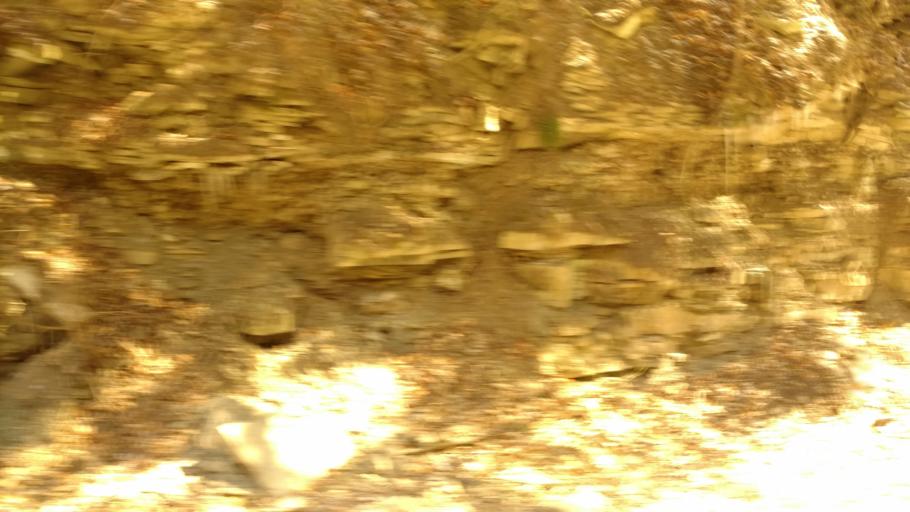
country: US
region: New York
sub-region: Allegany County
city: Wellsville
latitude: 42.0710
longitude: -77.9353
